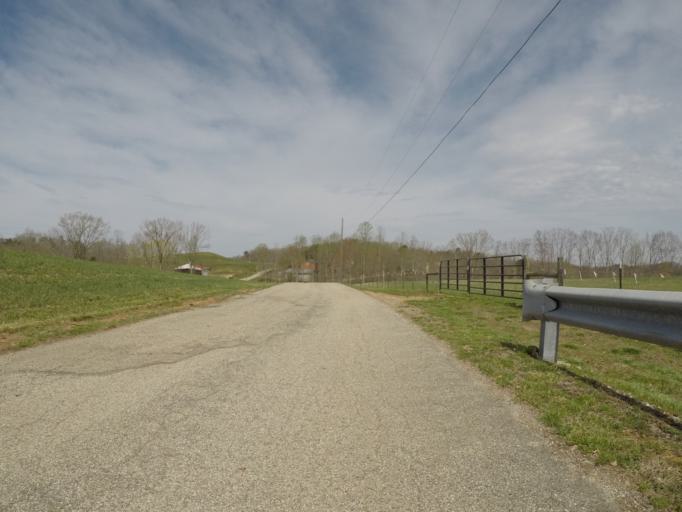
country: US
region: West Virginia
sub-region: Cabell County
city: Pea Ridge
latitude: 38.3264
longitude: -82.3529
